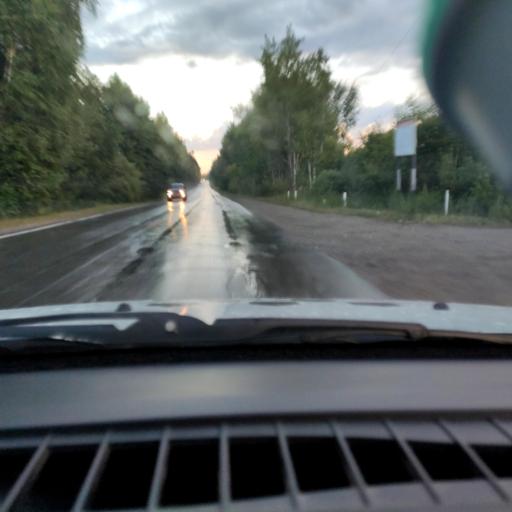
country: RU
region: Chelyabinsk
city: Ozersk
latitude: 55.8216
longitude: 60.6439
